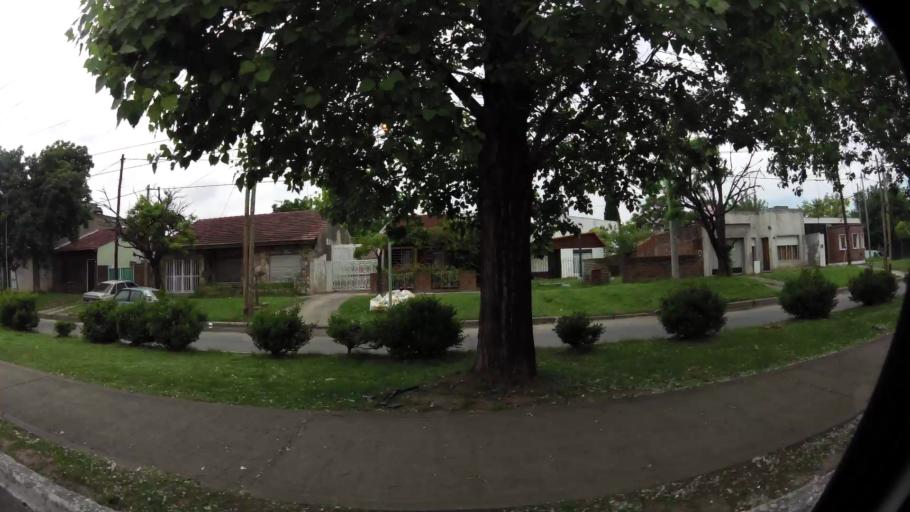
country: AR
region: Buenos Aires
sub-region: Partido de La Plata
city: La Plata
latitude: -34.9075
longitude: -57.9889
